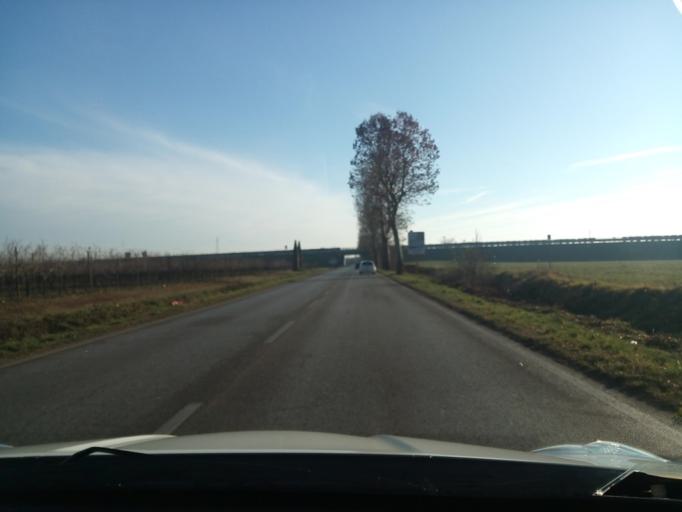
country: IT
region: Veneto
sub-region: Provincia di Vicenza
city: Villaverla
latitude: 45.6687
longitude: 11.4895
